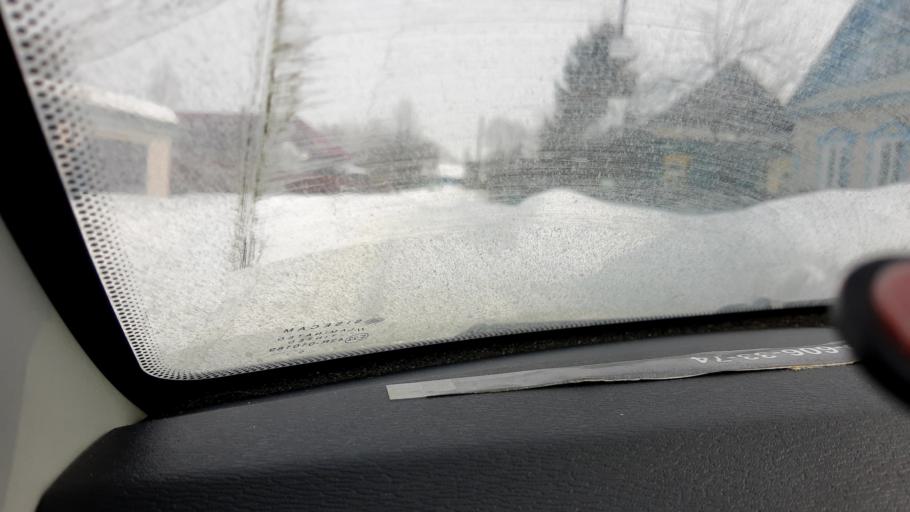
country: RU
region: Nizjnij Novgorod
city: Sitniki
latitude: 56.5290
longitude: 44.0583
